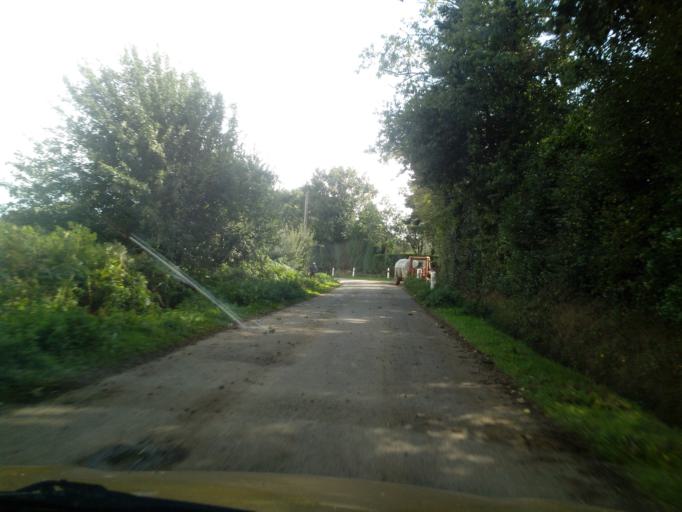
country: FR
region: Brittany
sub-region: Departement des Cotes-d'Armor
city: Merdrignac
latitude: 48.1387
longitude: -2.4009
